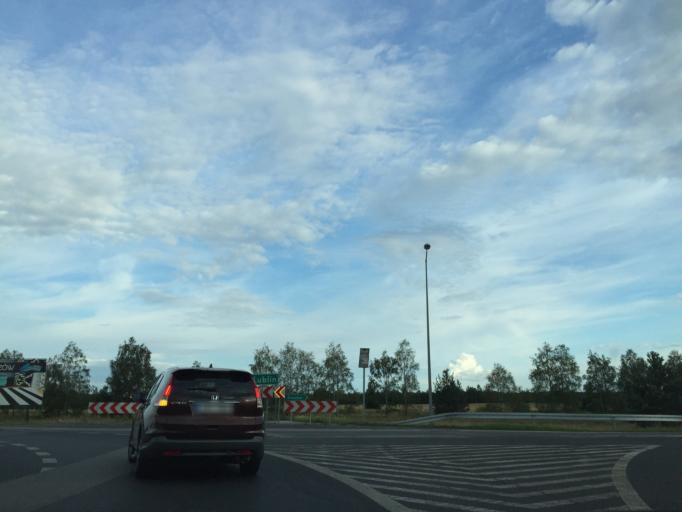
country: PL
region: Lublin Voivodeship
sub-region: Powiat lubartowski
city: Lubartow
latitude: 51.4334
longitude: 22.5957
